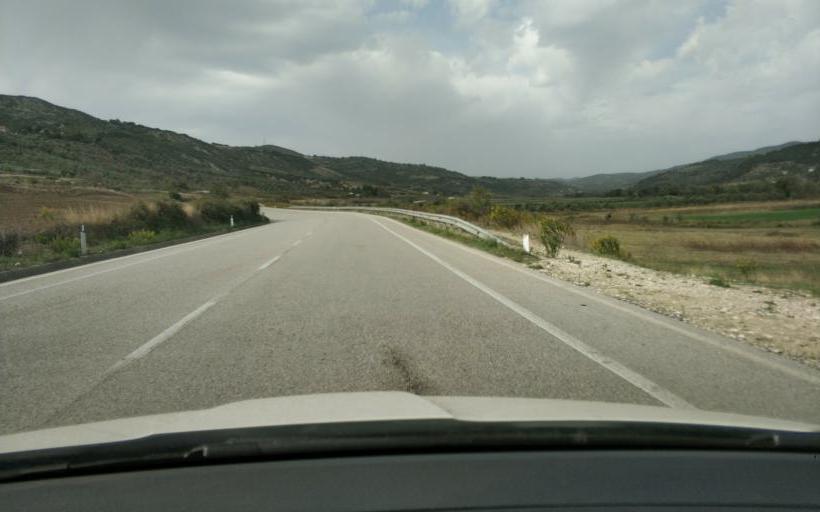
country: AL
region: Gjirokaster
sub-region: Rrethi i Tepelenes
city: Krahes
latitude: 40.4375
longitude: 19.8505
